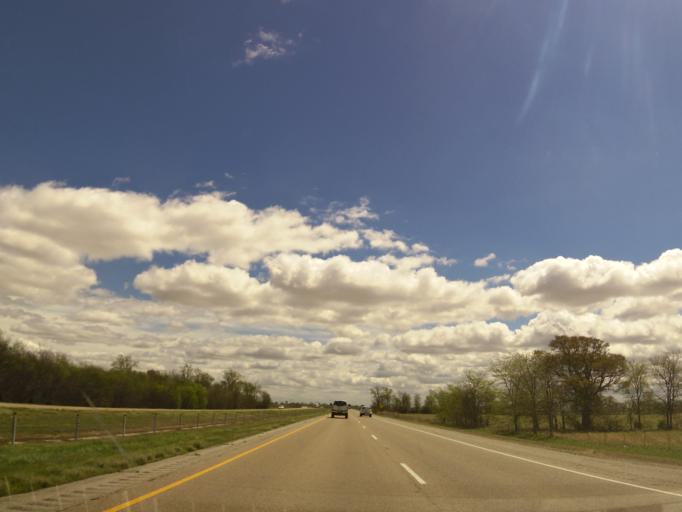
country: US
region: Arkansas
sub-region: Craighead County
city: Bay
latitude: 35.7815
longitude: -90.5963
